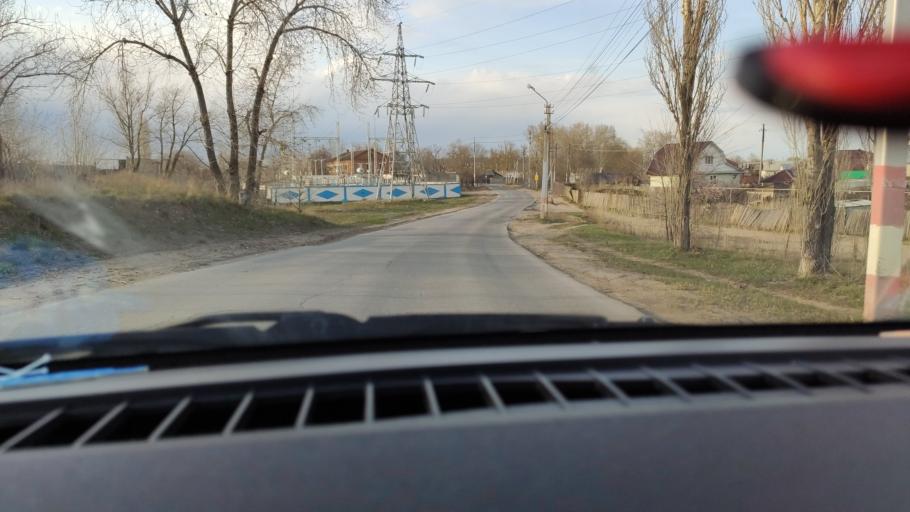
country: RU
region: Saratov
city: Engel's
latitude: 51.4922
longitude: 46.0527
